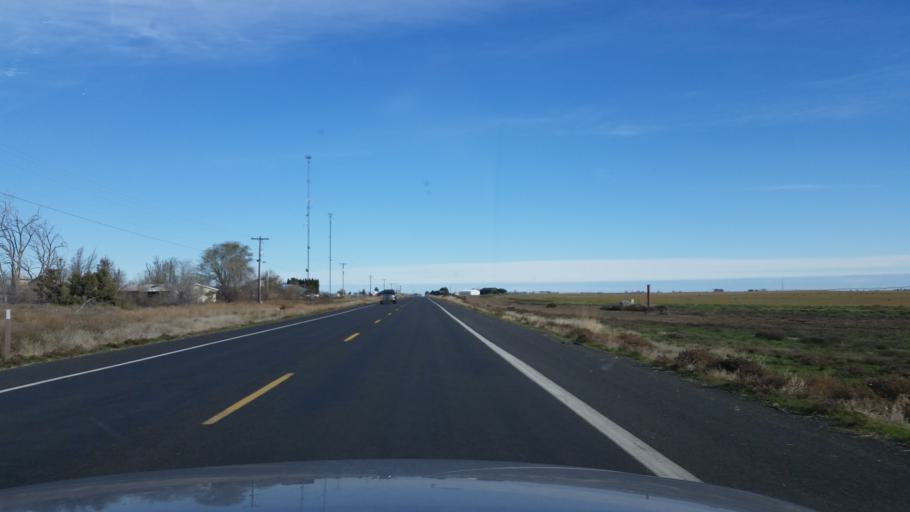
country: US
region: Washington
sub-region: Grant County
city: Quincy
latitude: 47.1064
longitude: -119.8271
